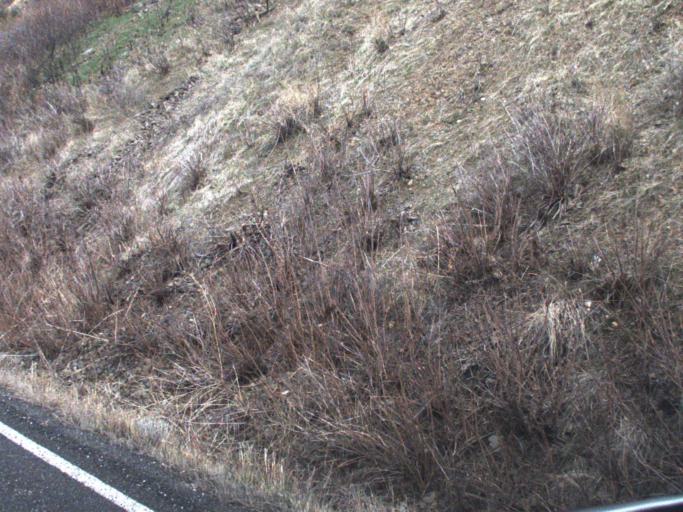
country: US
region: Washington
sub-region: Yakima County
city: Tieton
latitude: 46.7669
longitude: -120.8332
